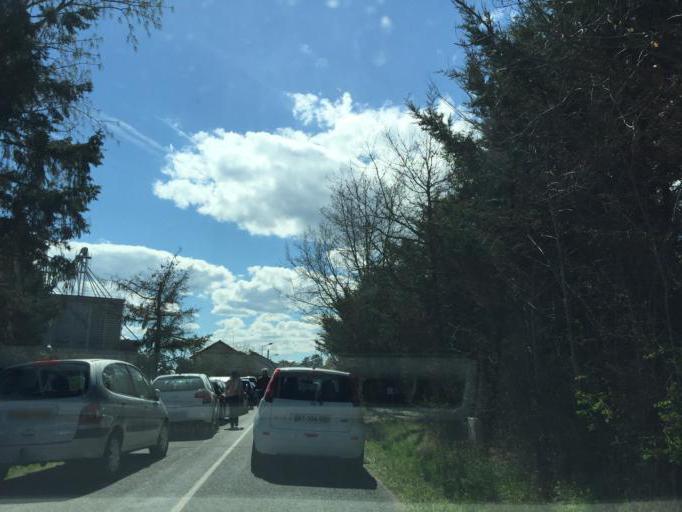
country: FR
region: Rhone-Alpes
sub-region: Departement de la Loire
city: Feurs
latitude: 45.6999
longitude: 4.1778
